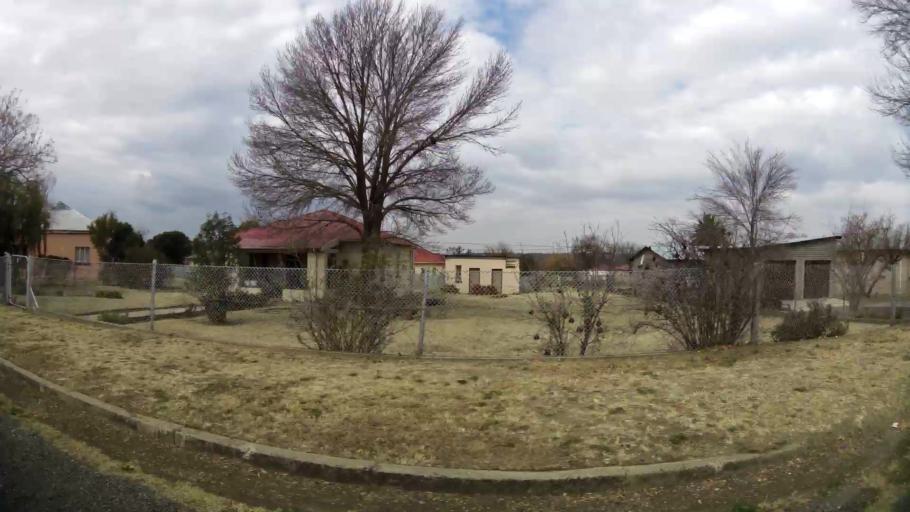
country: ZA
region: Orange Free State
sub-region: Fezile Dabi District Municipality
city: Kroonstad
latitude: -27.6527
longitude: 27.2369
